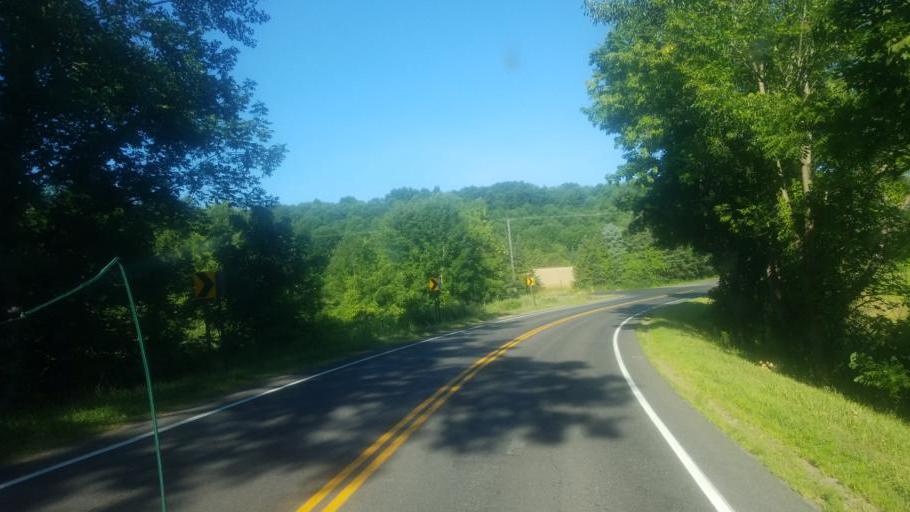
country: US
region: New York
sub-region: Wayne County
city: Newark
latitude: 43.0889
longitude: -77.0570
